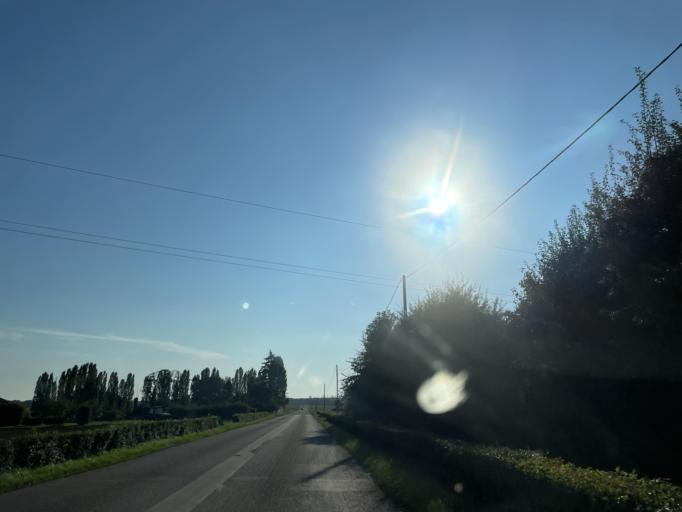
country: FR
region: Ile-de-France
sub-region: Departement de Seine-et-Marne
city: Voulangis
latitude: 48.8439
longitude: 2.8917
